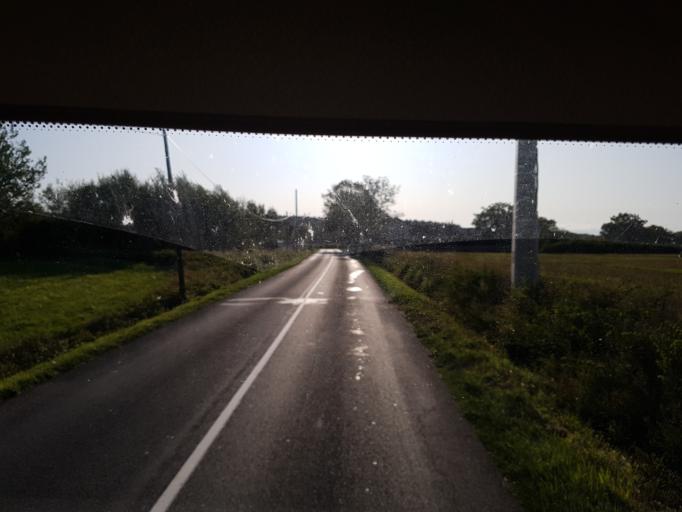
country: FR
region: Rhone-Alpes
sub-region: Departement de l'Ain
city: Priay
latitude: 46.0296
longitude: 5.2966
